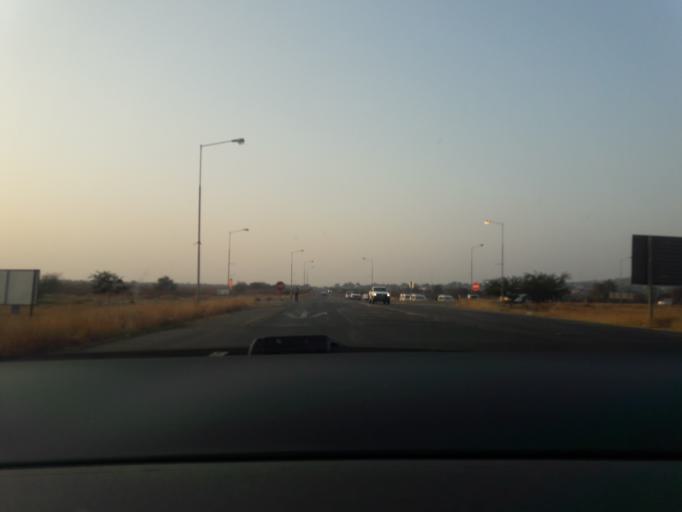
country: ZA
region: North-West
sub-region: Bojanala Platinum District Municipality
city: Mogwase
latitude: -25.4525
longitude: 27.3130
